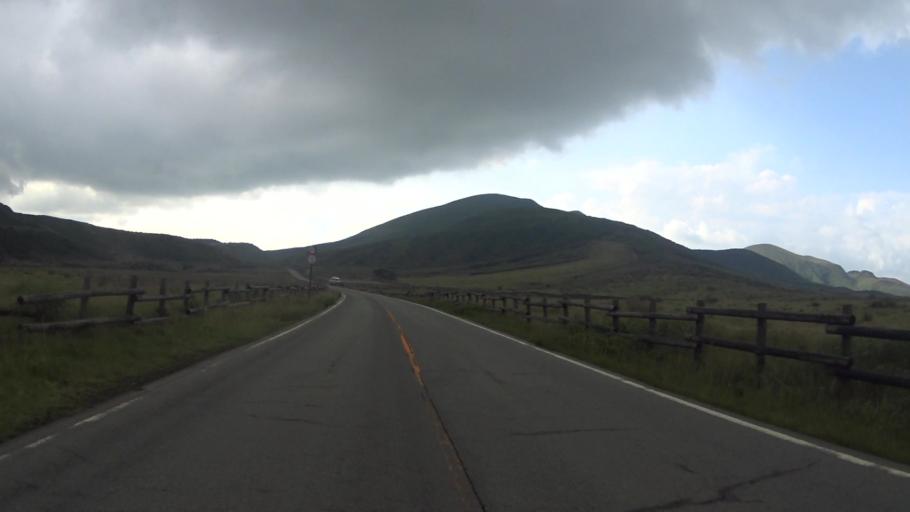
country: JP
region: Kumamoto
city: Aso
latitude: 32.8824
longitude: 131.0681
